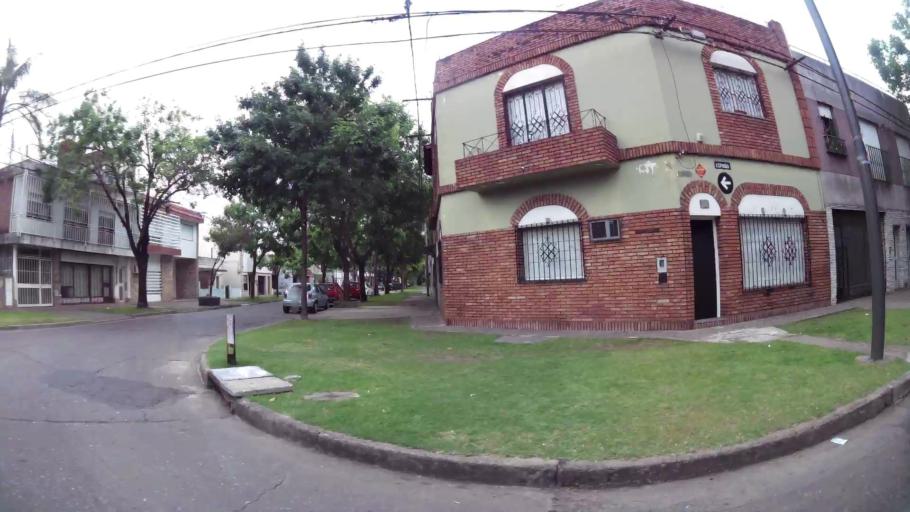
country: AR
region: Santa Fe
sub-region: Departamento de Rosario
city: Rosario
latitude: -32.9763
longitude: -60.6543
